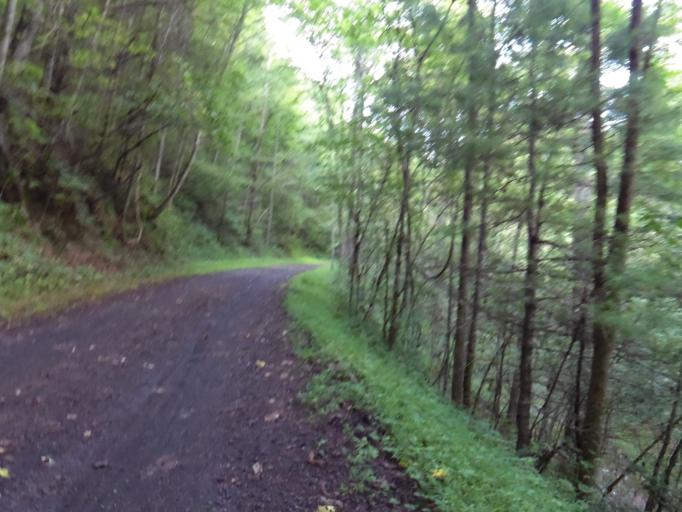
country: US
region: Virginia
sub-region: Washington County
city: Abingdon
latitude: 36.6841
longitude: -81.9443
